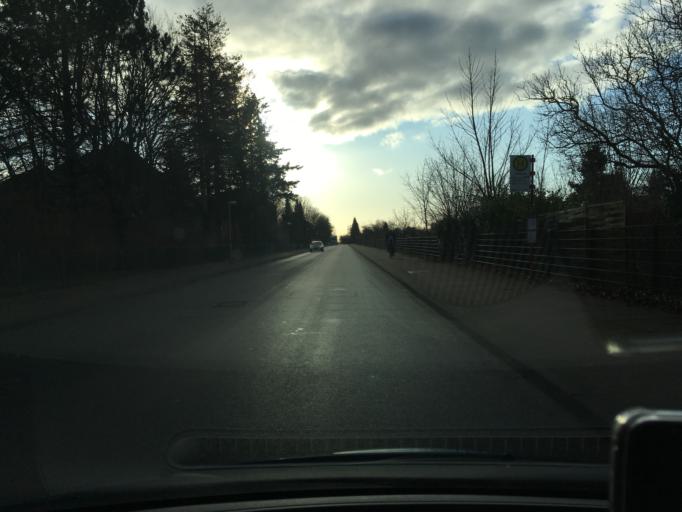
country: DE
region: Lower Saxony
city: Lueneburg
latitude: 53.2611
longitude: 10.3911
